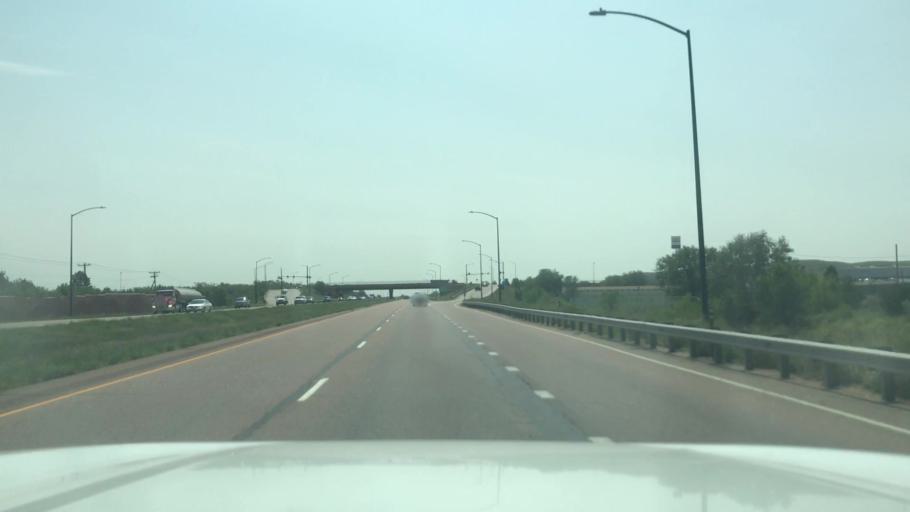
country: US
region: Colorado
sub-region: El Paso County
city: Fountain
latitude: 38.6765
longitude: -104.7120
